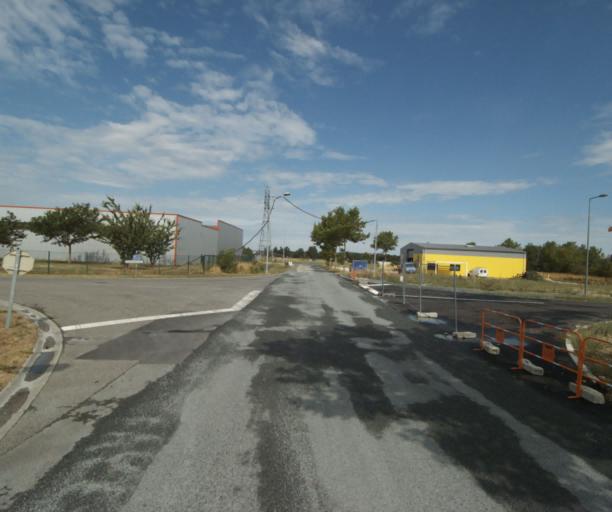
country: FR
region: Midi-Pyrenees
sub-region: Departement de la Haute-Garonne
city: Revel
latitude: 43.4592
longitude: 1.9818
